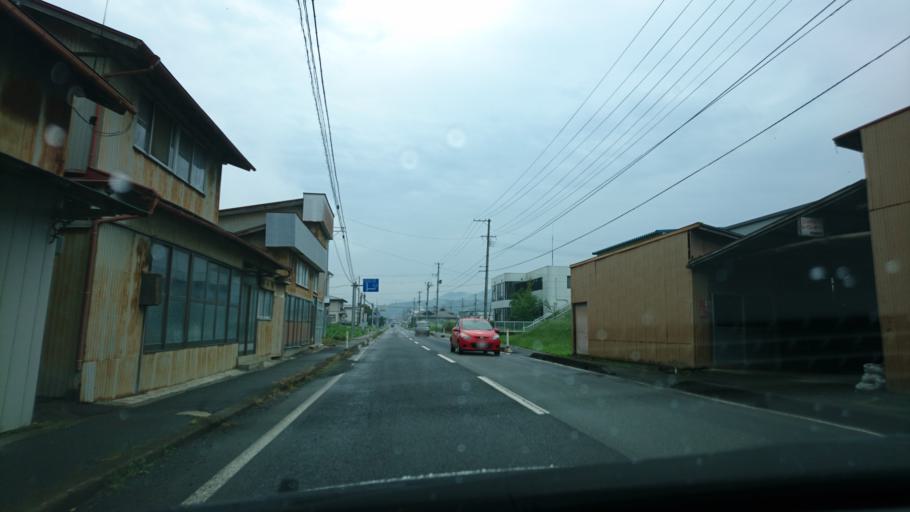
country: JP
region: Iwate
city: Ichinoseki
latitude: 38.9008
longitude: 141.2689
